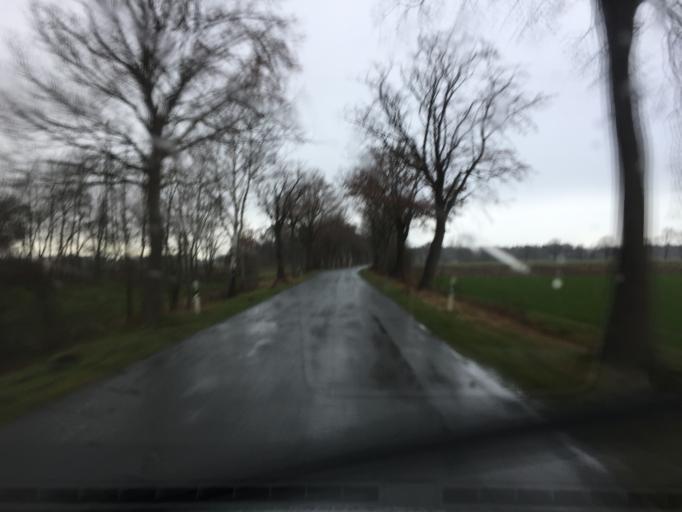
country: DE
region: Lower Saxony
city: Barenburg
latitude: 52.6485
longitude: 8.8208
